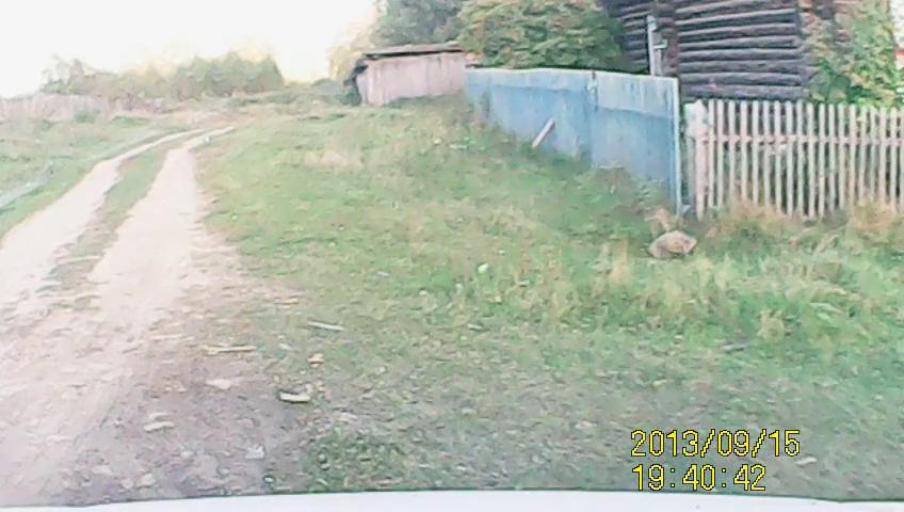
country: RU
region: Chelyabinsk
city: Kyshtym
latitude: 55.8476
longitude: 60.4825
